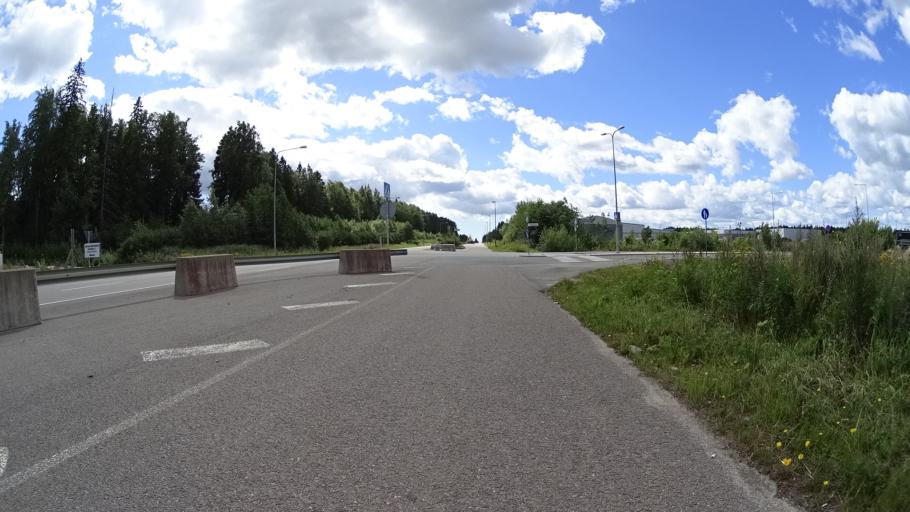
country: FI
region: Uusimaa
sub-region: Helsinki
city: Vantaa
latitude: 60.3300
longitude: 24.9227
